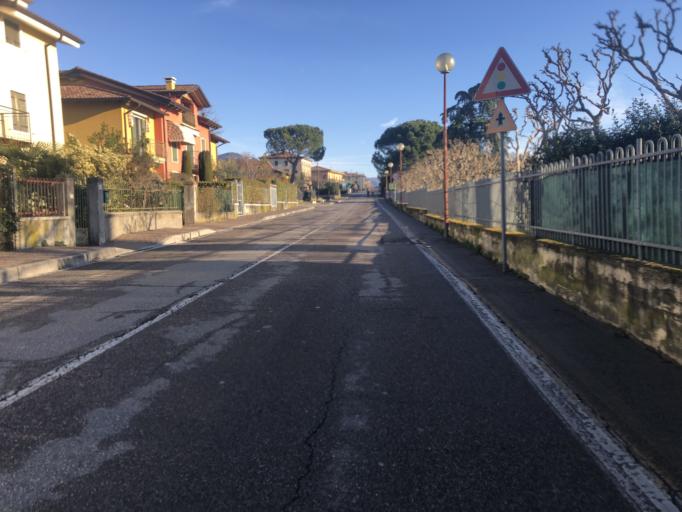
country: IT
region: Veneto
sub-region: Provincia di Verona
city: Pescantina
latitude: 45.4879
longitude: 10.8693
